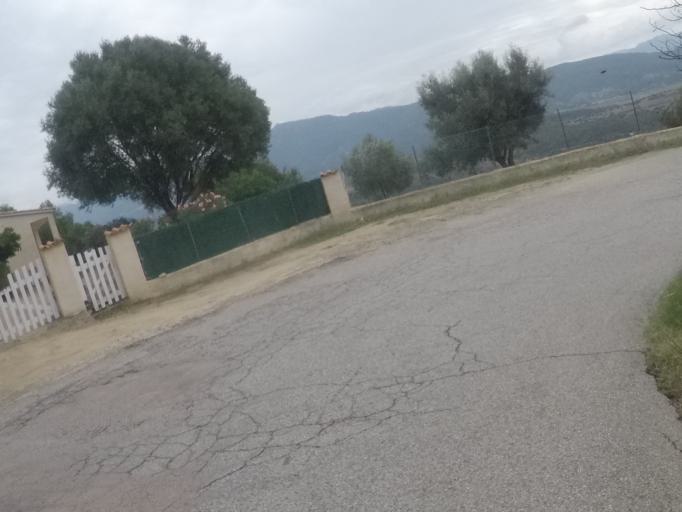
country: FR
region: Corsica
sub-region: Departement de la Corse-du-Sud
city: Pietrosella
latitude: 41.7549
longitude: 8.8142
